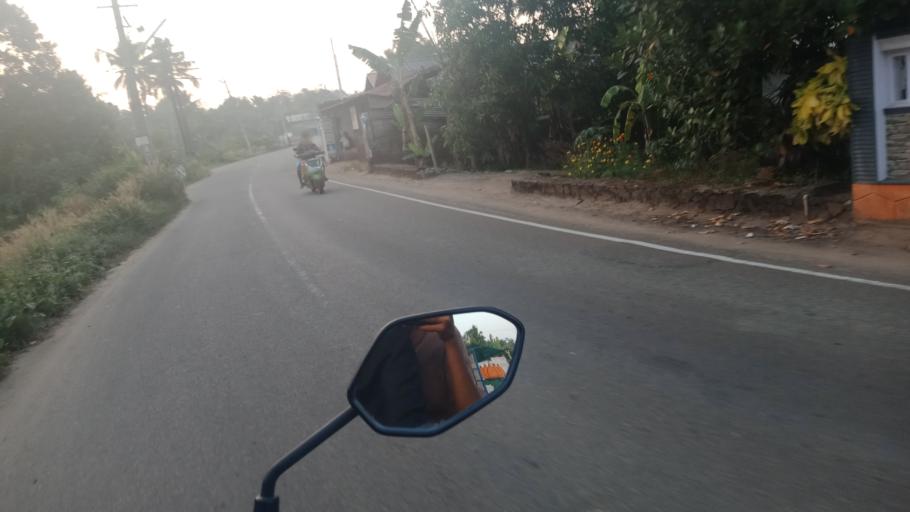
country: IN
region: Kerala
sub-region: Ernakulam
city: Angamali
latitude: 10.2003
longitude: 76.3023
